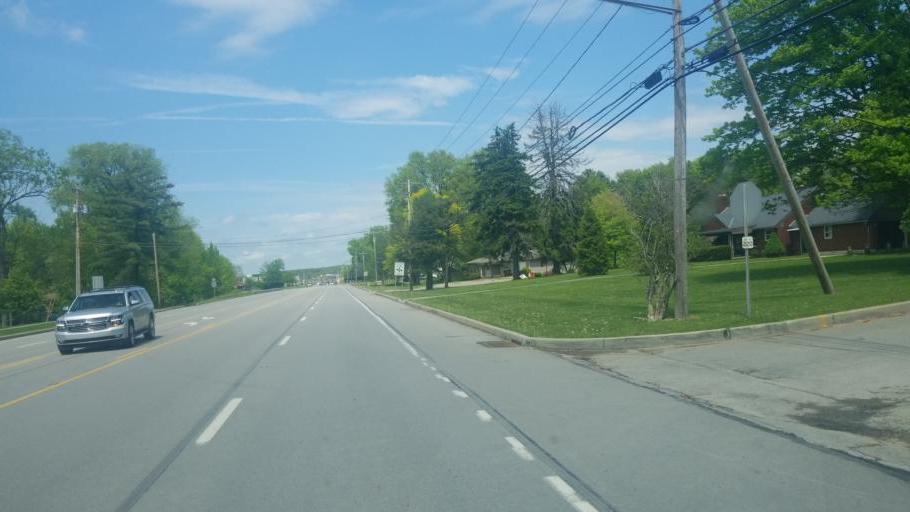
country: US
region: Pennsylvania
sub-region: Mercer County
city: Hermitage
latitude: 41.2213
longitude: -80.4537
